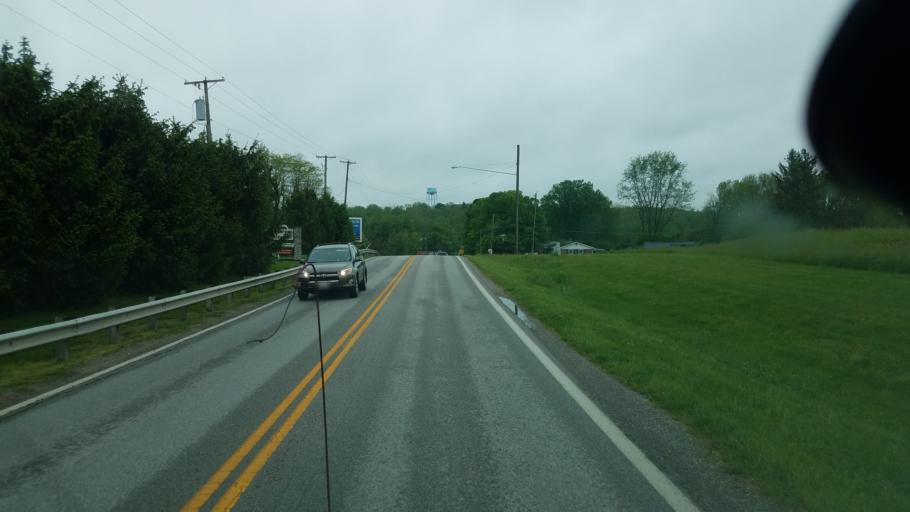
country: US
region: Ohio
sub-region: Highland County
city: Hillsboro
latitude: 39.2189
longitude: -83.6177
